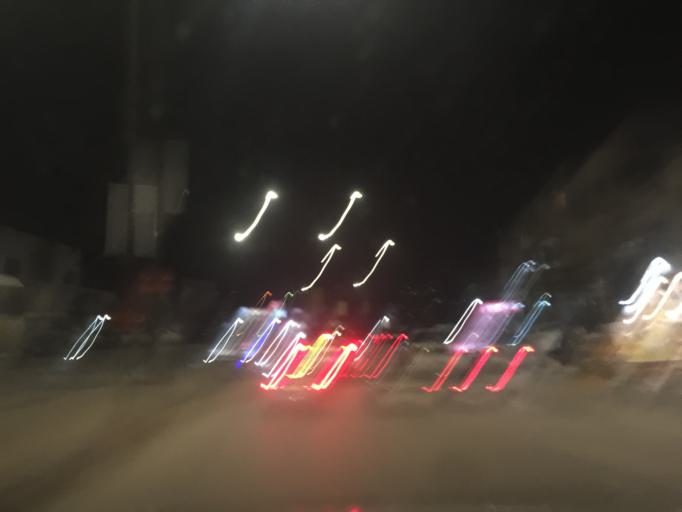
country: JO
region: Zarqa
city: Russeifa
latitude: 32.0217
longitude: 36.0163
